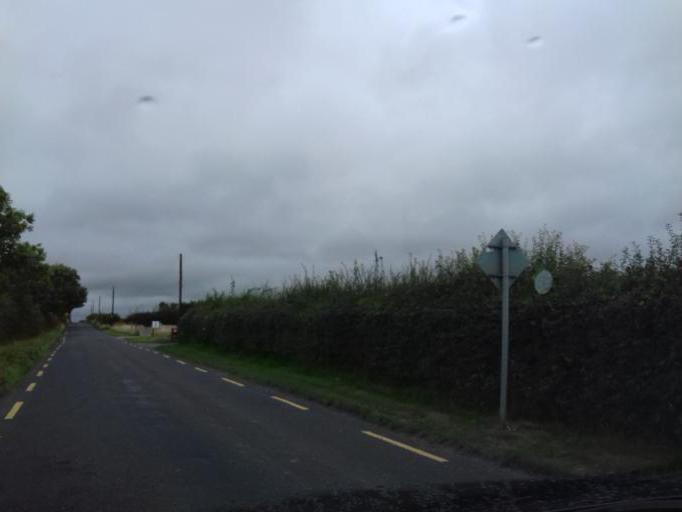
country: IE
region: Leinster
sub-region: Kilkenny
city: Graiguenamanagh
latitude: 52.6112
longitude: -7.0303
